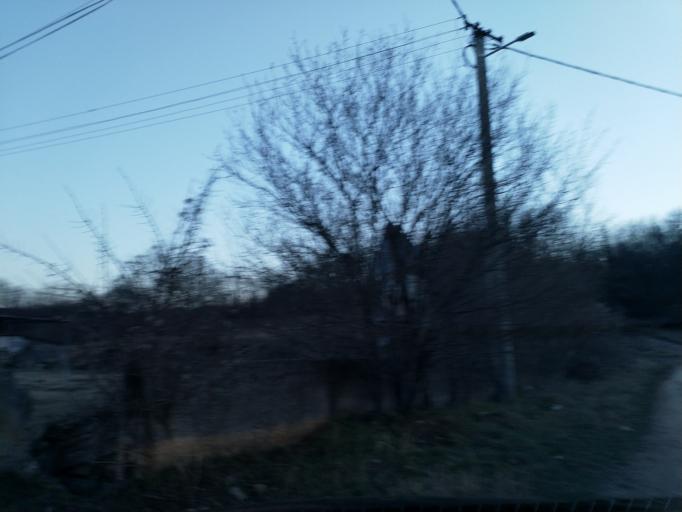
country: RS
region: Central Serbia
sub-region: Pomoravski Okrug
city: Paracin
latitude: 43.8612
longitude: 21.4729
